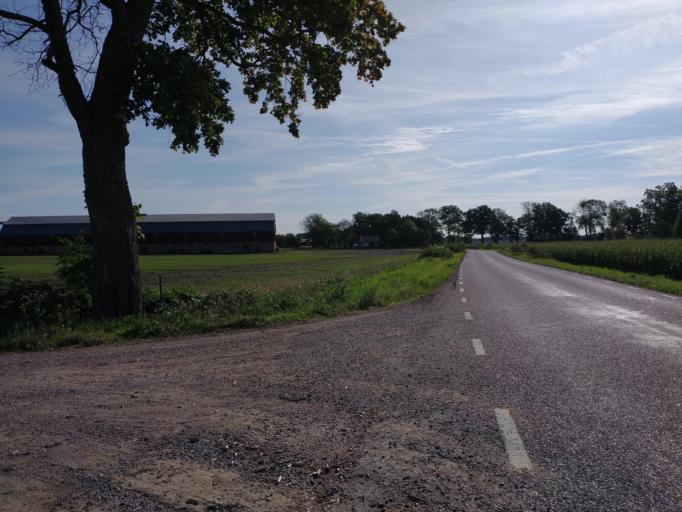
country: SE
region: Kalmar
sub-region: Kalmar Kommun
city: Lindsdal
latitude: 56.7863
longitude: 16.3200
